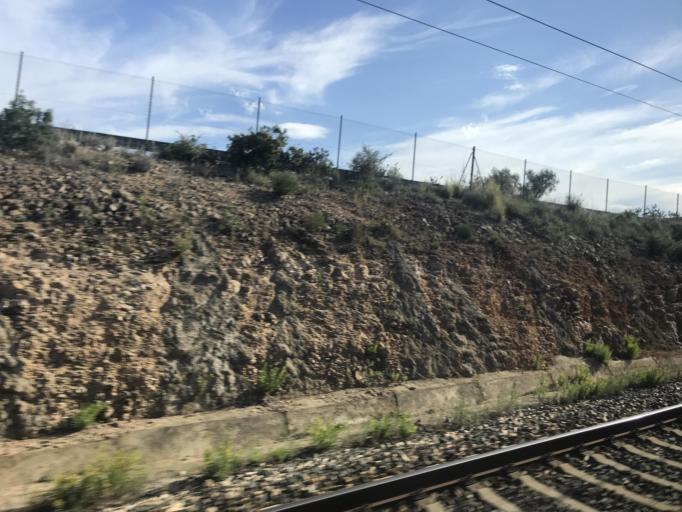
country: ES
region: Catalonia
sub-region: Provincia de Tarragona
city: L'Ampolla
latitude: 40.8212
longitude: 0.7236
